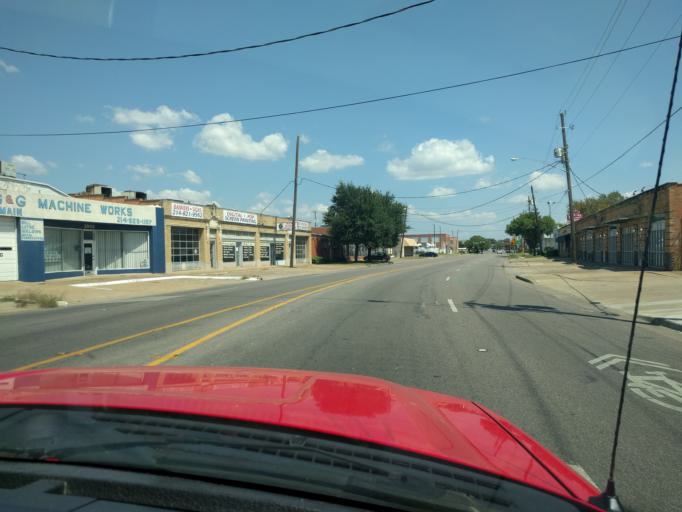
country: US
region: Texas
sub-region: Dallas County
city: Dallas
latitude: 32.7867
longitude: -96.7729
